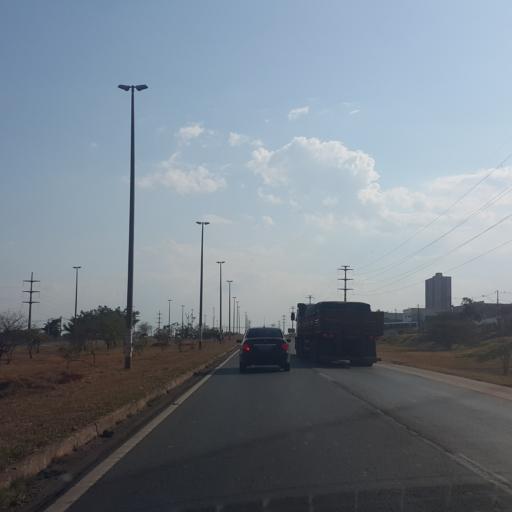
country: BR
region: Federal District
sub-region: Brasilia
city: Brasilia
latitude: -15.8876
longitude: -48.0786
